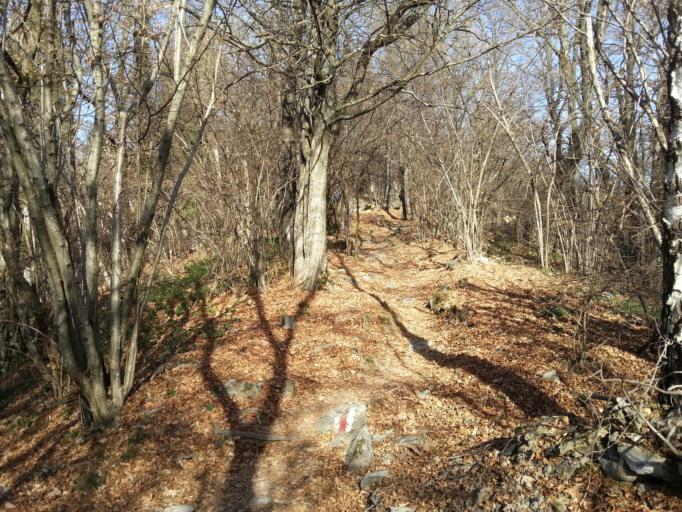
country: IT
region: Lombardy
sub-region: Provincia di Como
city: Maslianico
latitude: 45.8595
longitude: 9.0487
